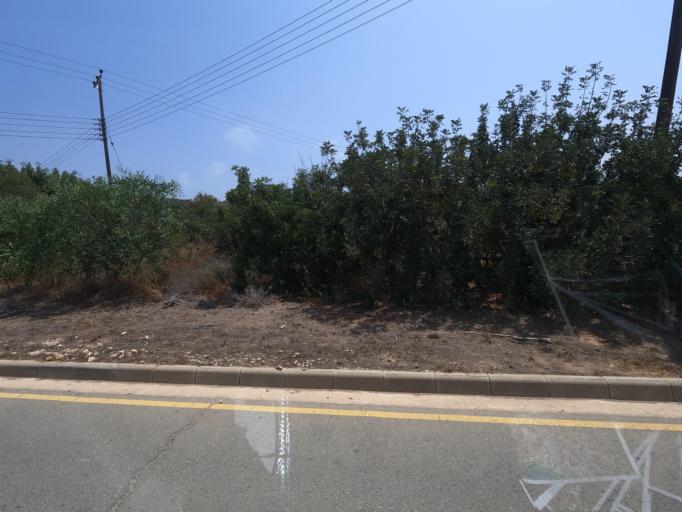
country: CY
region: Ammochostos
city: Ayia Napa
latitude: 34.9814
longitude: 34.0234
